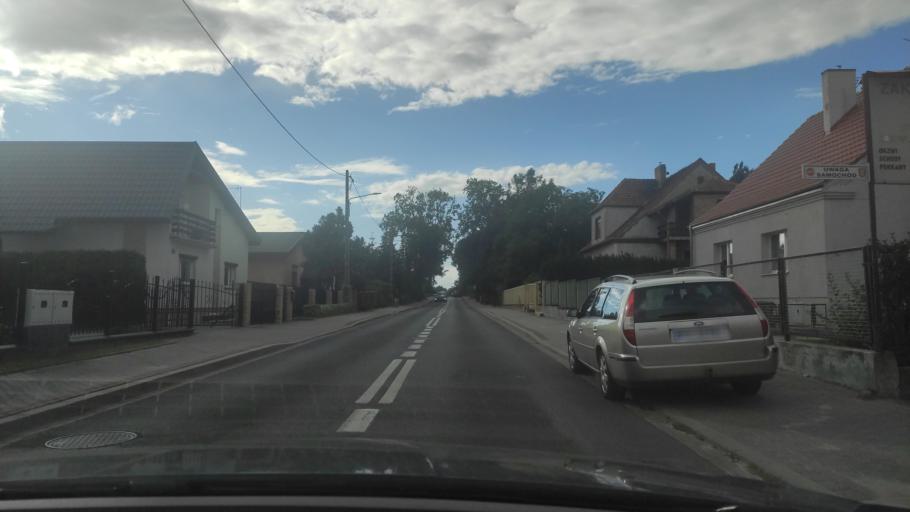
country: PL
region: Greater Poland Voivodeship
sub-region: Powiat poznanski
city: Swarzedz
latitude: 52.4092
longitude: 17.0656
